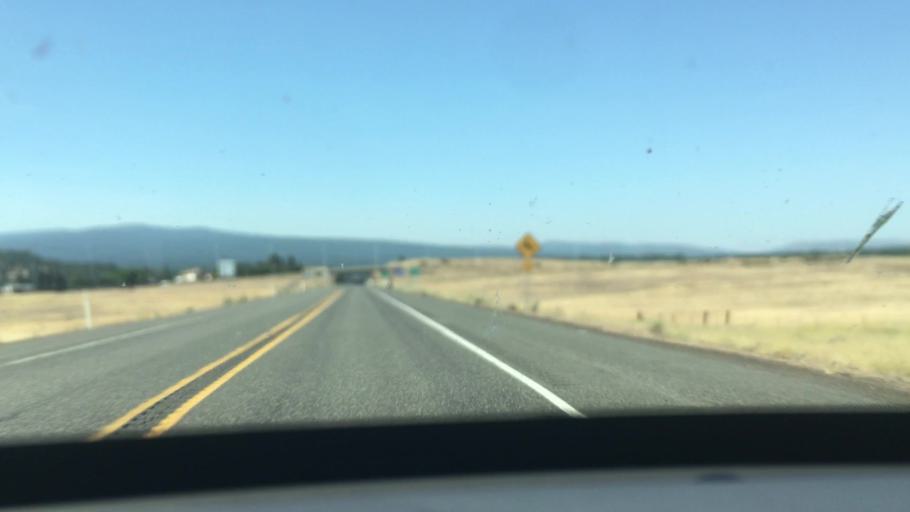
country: US
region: Washington
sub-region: Klickitat County
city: Goldendale
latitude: 45.8142
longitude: -120.8068
